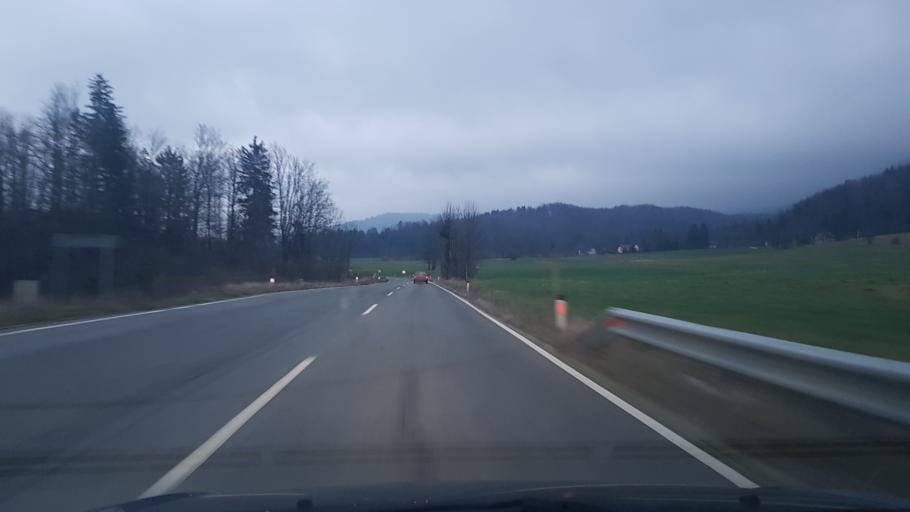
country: SI
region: Idrija
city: Idrija
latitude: 45.9252
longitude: 14.0539
